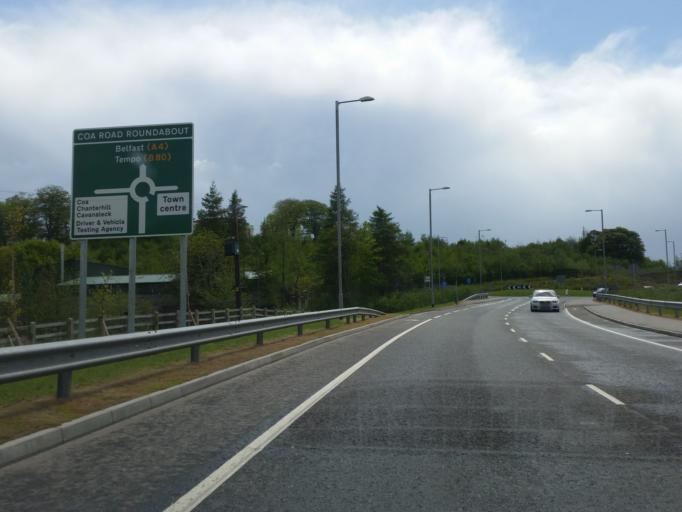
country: GB
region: Northern Ireland
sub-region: Fermanagh District
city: Enniskillen
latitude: 54.3553
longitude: -7.6193
